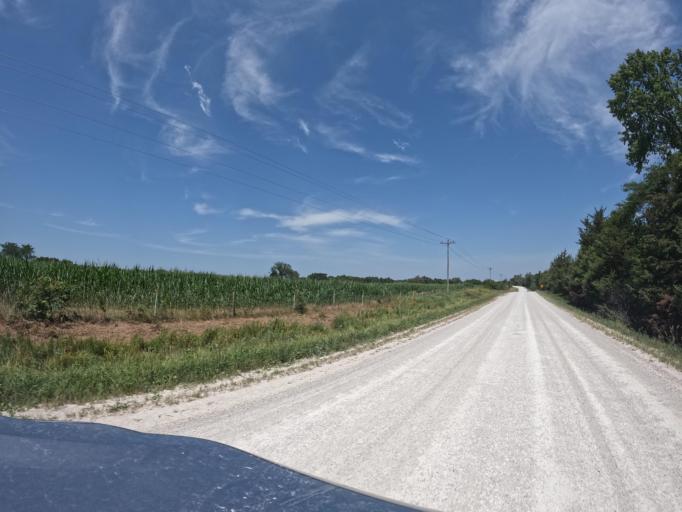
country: US
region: Iowa
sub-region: Henry County
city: Mount Pleasant
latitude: 40.9013
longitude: -91.5361
